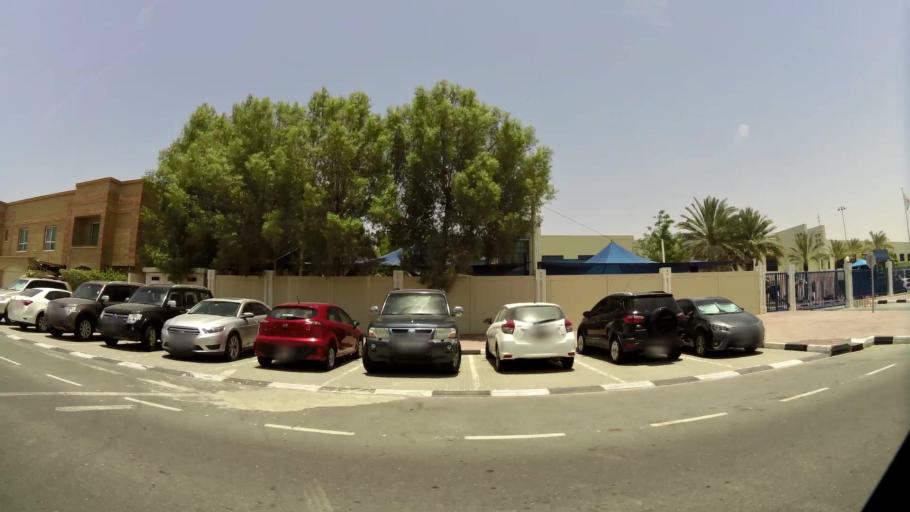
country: AE
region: Dubai
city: Dubai
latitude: 25.1758
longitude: 55.2376
